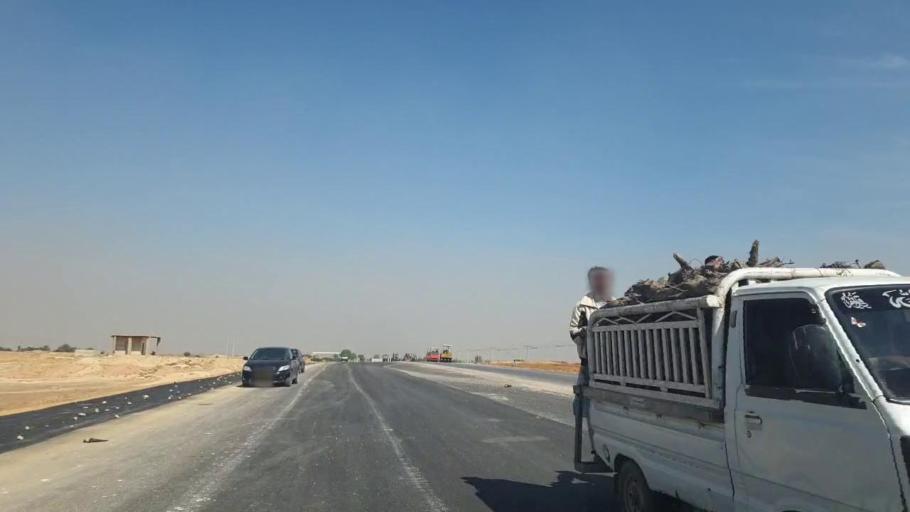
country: PK
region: Sindh
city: Jamshoro
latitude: 25.5283
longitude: 68.2793
